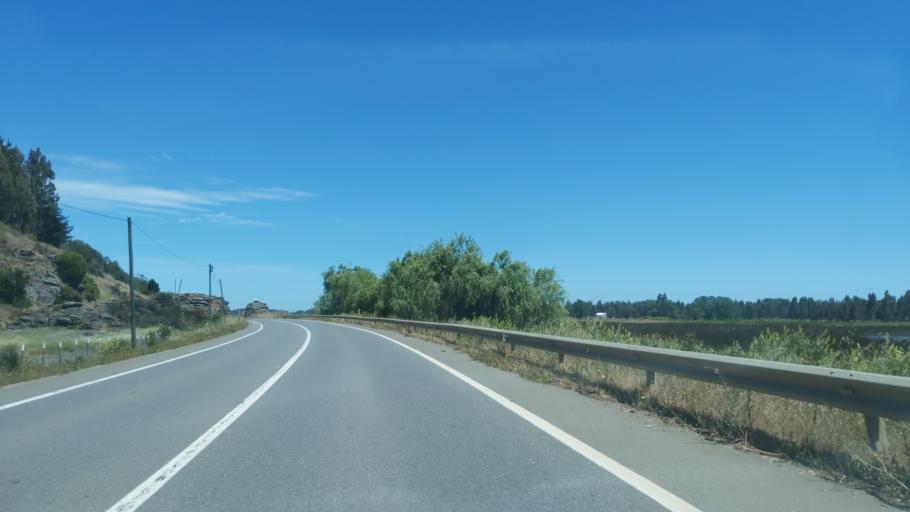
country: CL
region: Maule
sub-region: Provincia de Talca
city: Constitucion
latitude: -35.1541
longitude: -72.2429
